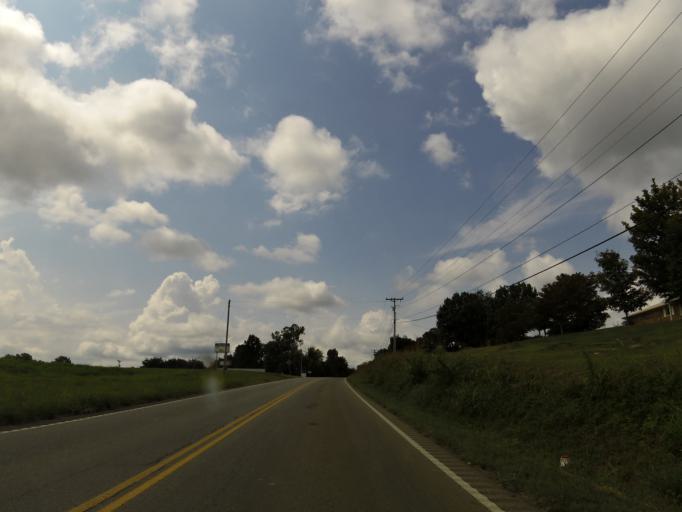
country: US
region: Tennessee
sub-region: Perry County
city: Linden
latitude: 35.6350
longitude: -87.8291
